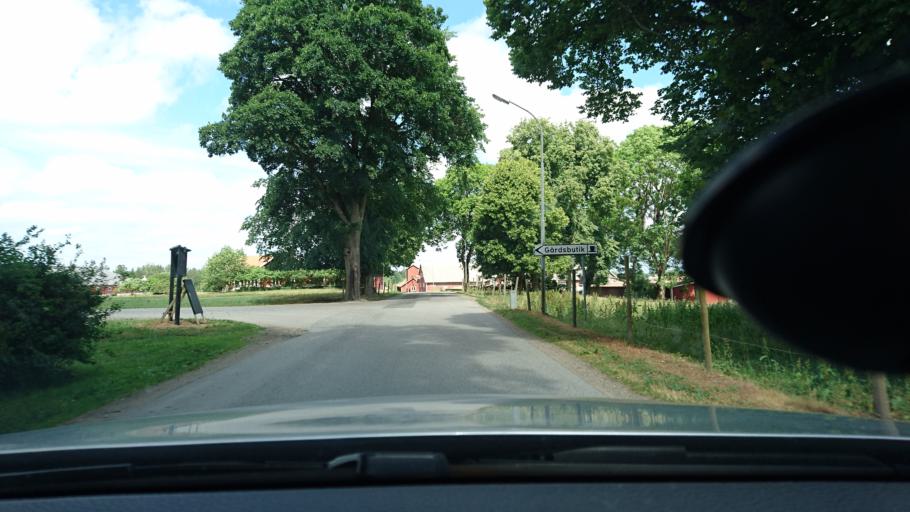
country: SE
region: Kronoberg
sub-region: Alvesta Kommun
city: Moheda
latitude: 56.9495
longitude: 14.5712
